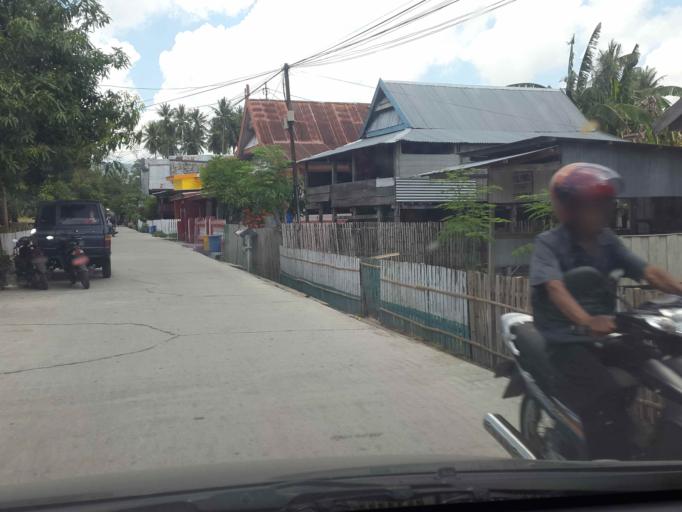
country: ID
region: South Sulawesi
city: Bantaeng
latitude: -6.1106
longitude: 120.4661
